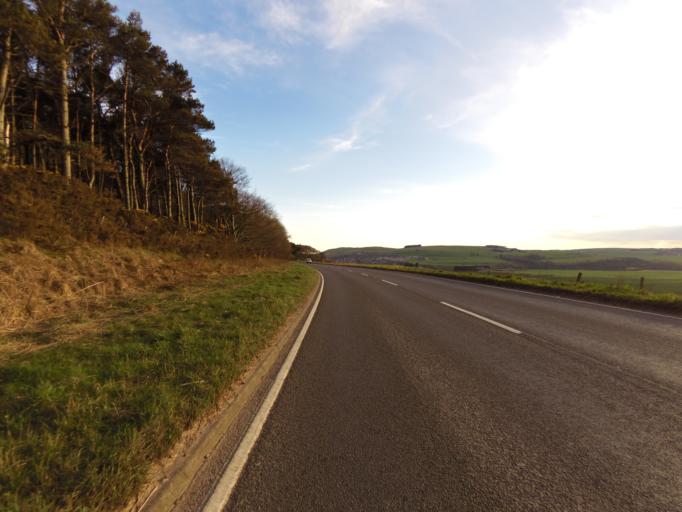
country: GB
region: Scotland
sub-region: Aberdeenshire
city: Inverbervie
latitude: 56.8575
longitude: -2.2690
